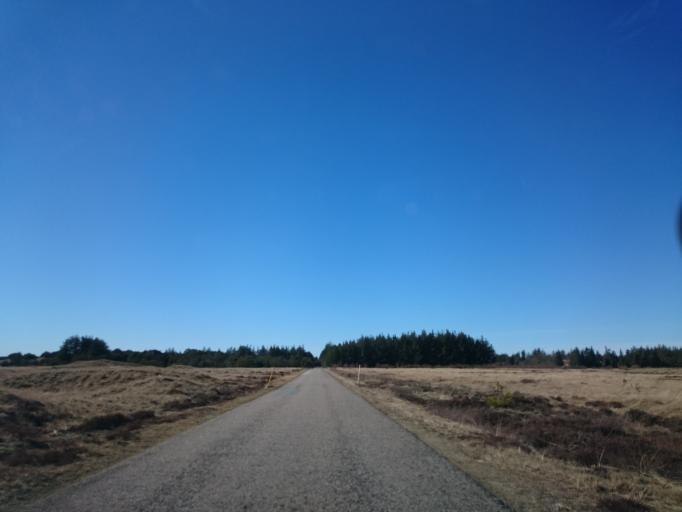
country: DK
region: North Denmark
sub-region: Frederikshavn Kommune
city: Strandby
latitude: 57.6248
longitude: 10.3410
